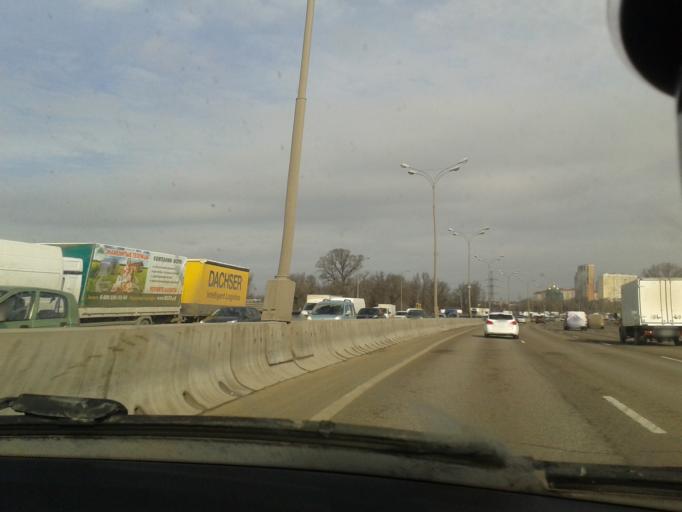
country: RU
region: Moscow
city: Strogino
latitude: 55.8447
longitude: 37.3924
